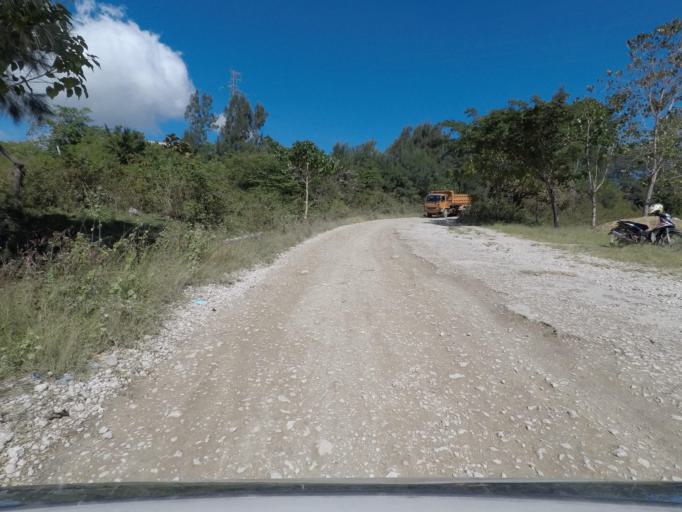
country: TL
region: Baucau
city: Venilale
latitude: -8.6676
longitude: 126.3693
